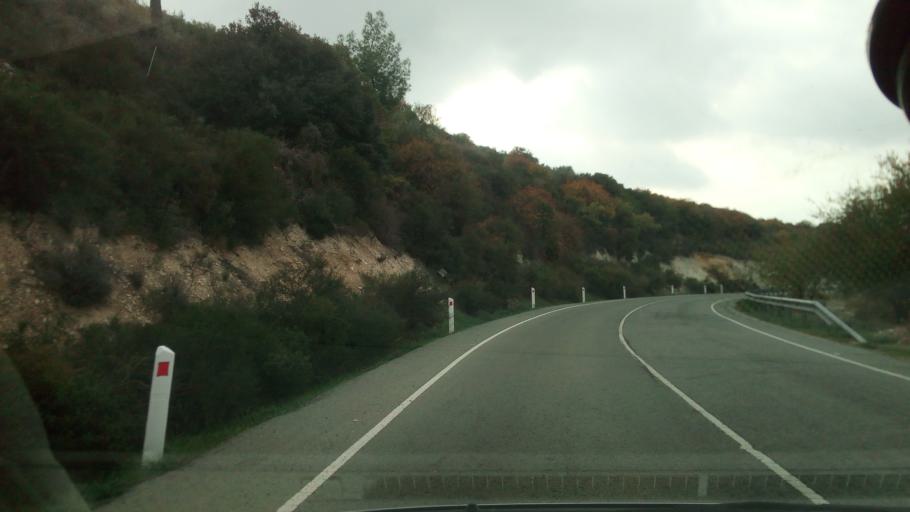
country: CY
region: Lefkosia
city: Lythrodontas
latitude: 34.8714
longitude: 33.2926
